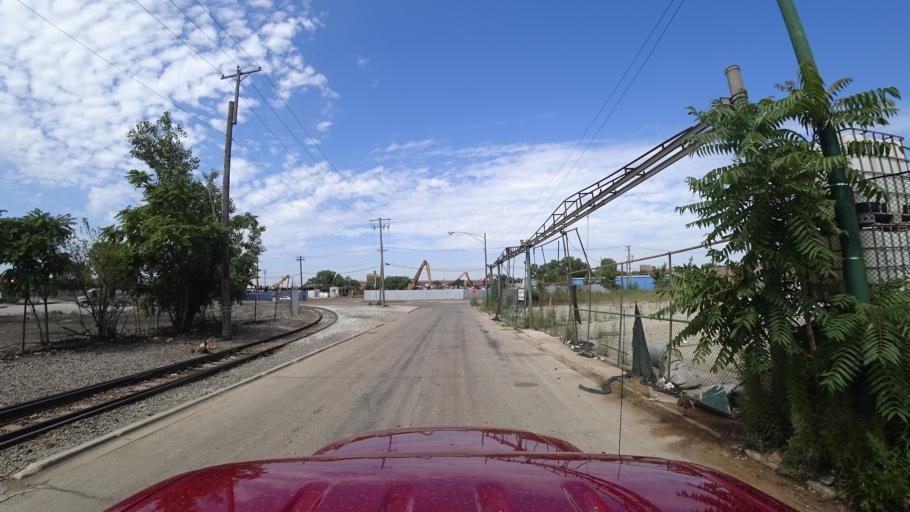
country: US
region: Illinois
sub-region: Cook County
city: Chicago
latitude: 41.8253
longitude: -87.6547
